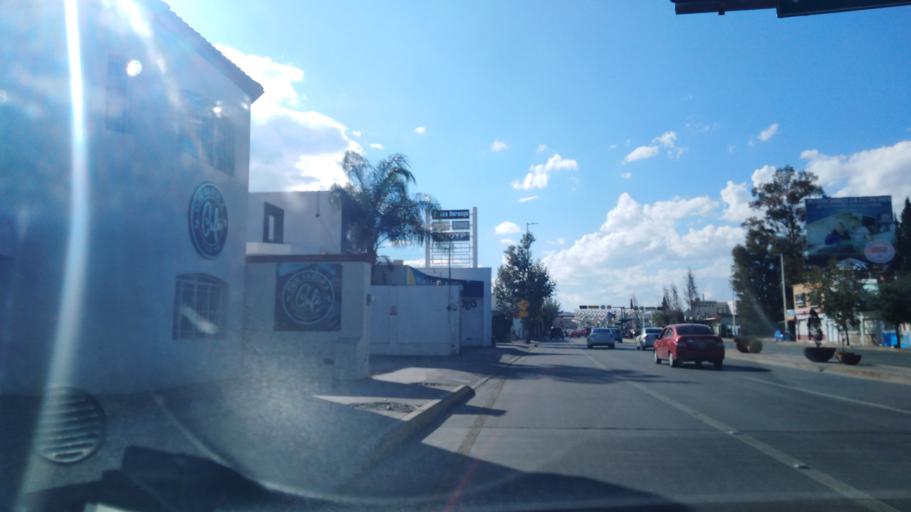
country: MX
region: Durango
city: Victoria de Durango
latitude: 24.0345
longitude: -104.6735
